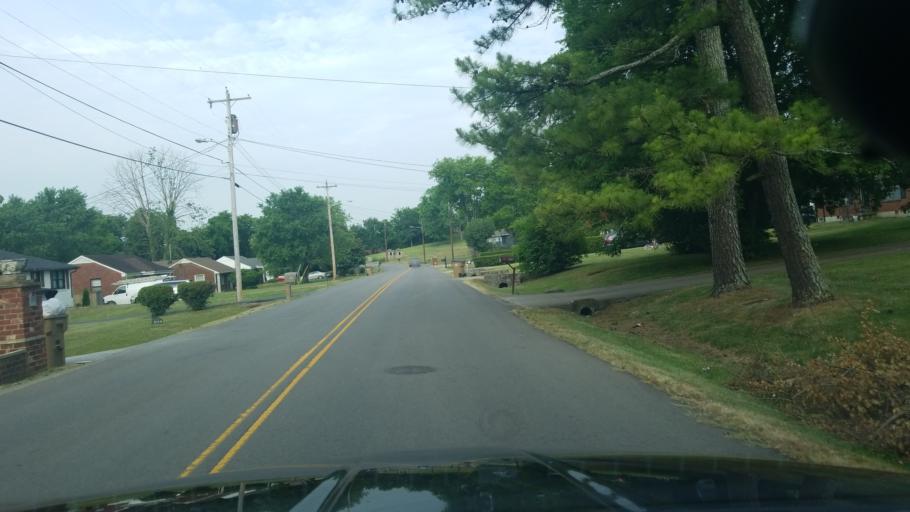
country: US
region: Tennessee
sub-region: Davidson County
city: Goodlettsville
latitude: 36.2643
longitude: -86.7533
